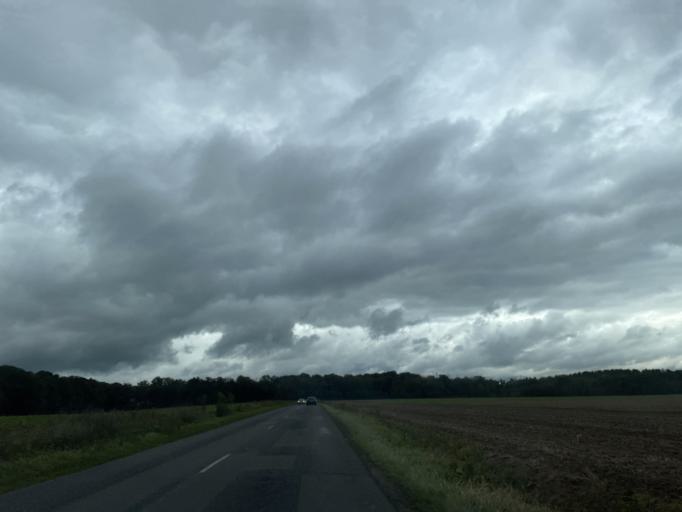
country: FR
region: Ile-de-France
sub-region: Departement de Seine-et-Marne
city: Sammeron
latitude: 48.8886
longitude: 3.0671
